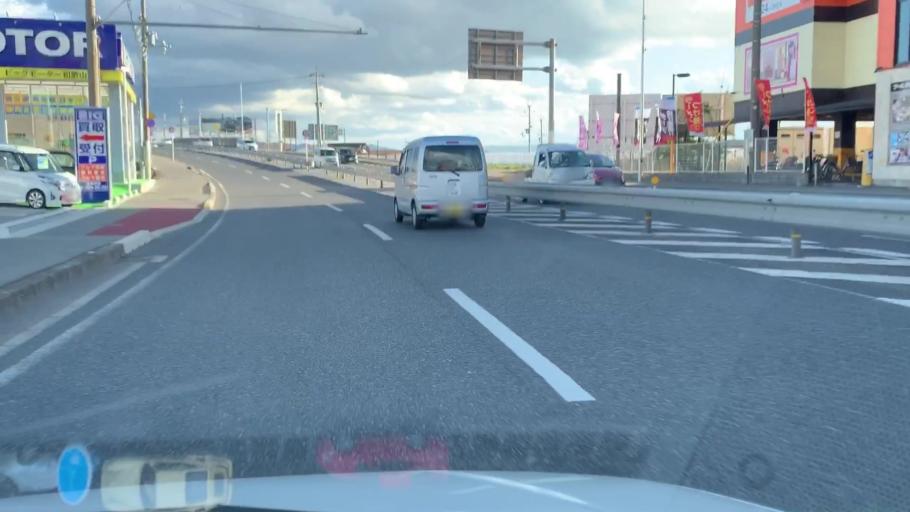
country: JP
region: Wakayama
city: Wakayama-shi
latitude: 34.2344
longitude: 135.1542
